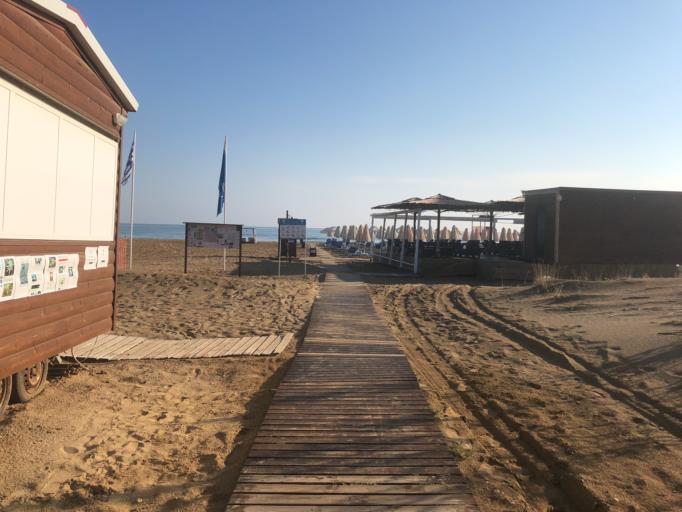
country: GR
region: Crete
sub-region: Nomos Chanias
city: Georgioupolis
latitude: 35.3547
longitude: 24.2860
